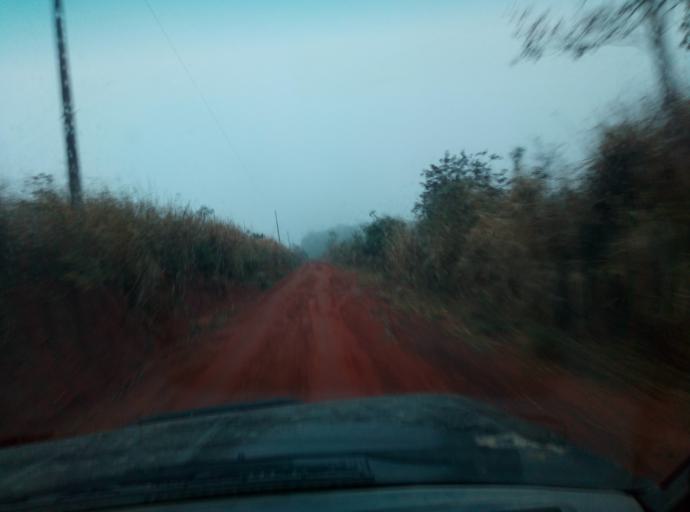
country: PY
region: Caaguazu
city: Doctor Cecilio Baez
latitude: -25.1589
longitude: -56.2644
